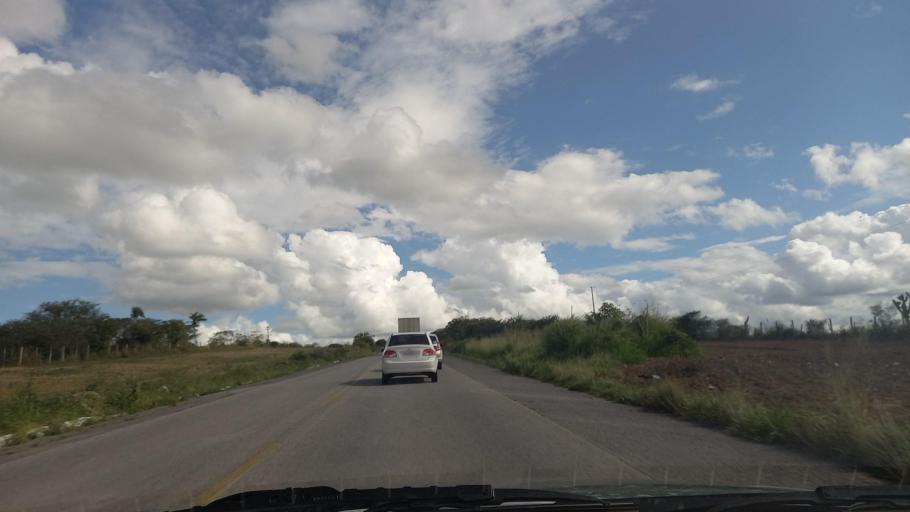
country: BR
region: Pernambuco
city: Garanhuns
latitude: -8.7991
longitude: -36.4384
